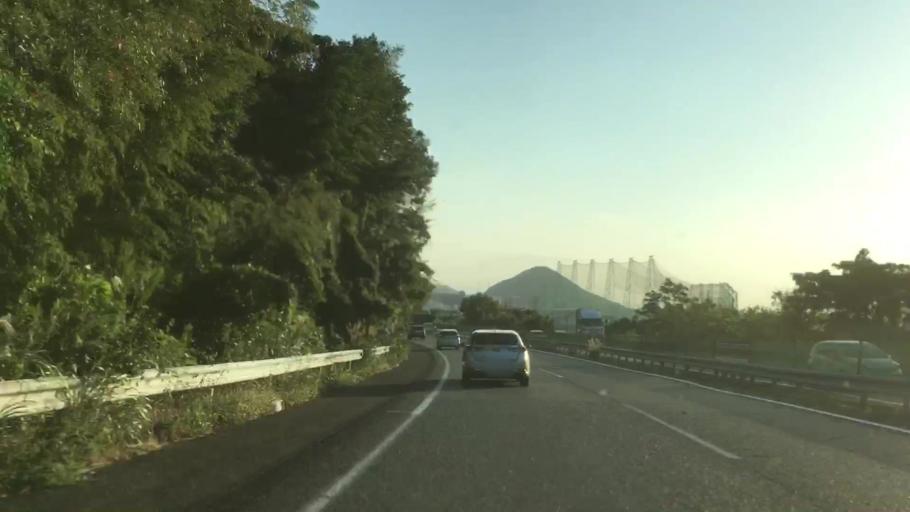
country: JP
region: Yamaguchi
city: Shimonoseki
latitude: 34.0205
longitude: 130.9587
